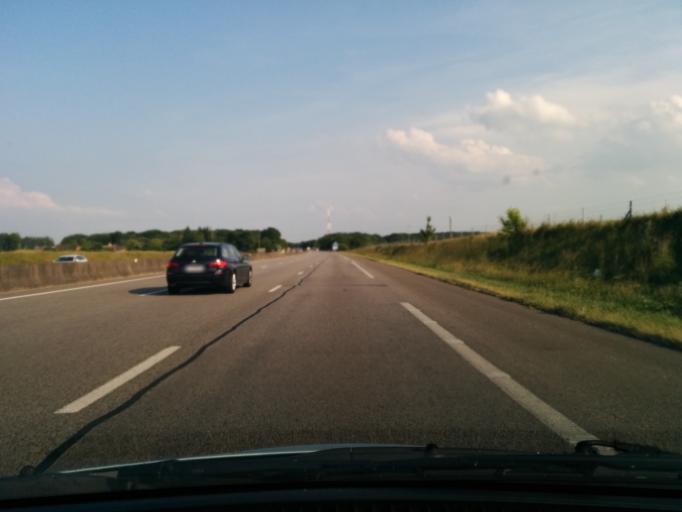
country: FR
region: Haute-Normandie
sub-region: Departement de l'Eure
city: Saint-Aubin-sur-Gaillon
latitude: 49.1120
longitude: 1.3368
